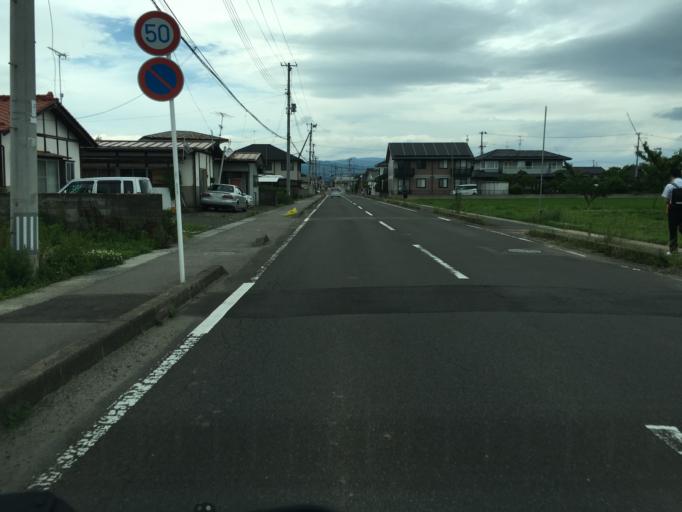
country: JP
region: Fukushima
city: Fukushima-shi
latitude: 37.7741
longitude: 140.4352
